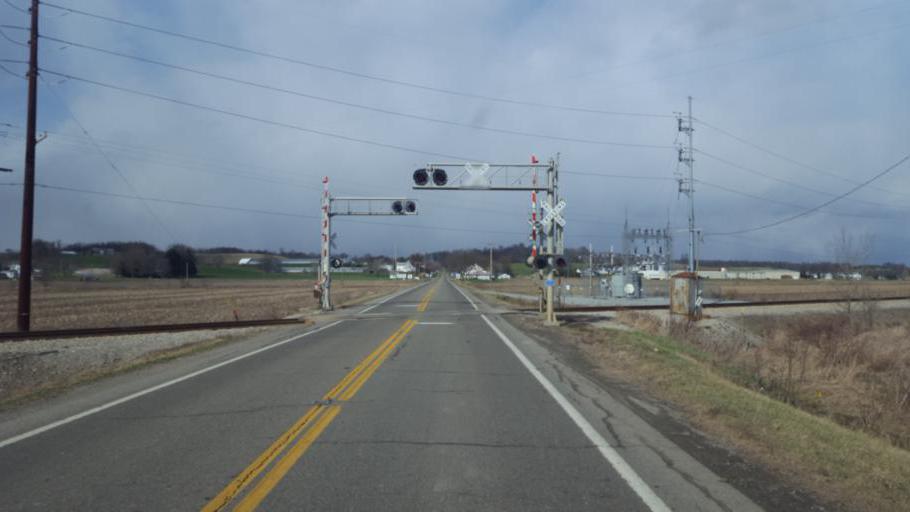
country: US
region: Ohio
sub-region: Tuscarawas County
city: Sugarcreek
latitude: 40.4698
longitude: -81.6785
